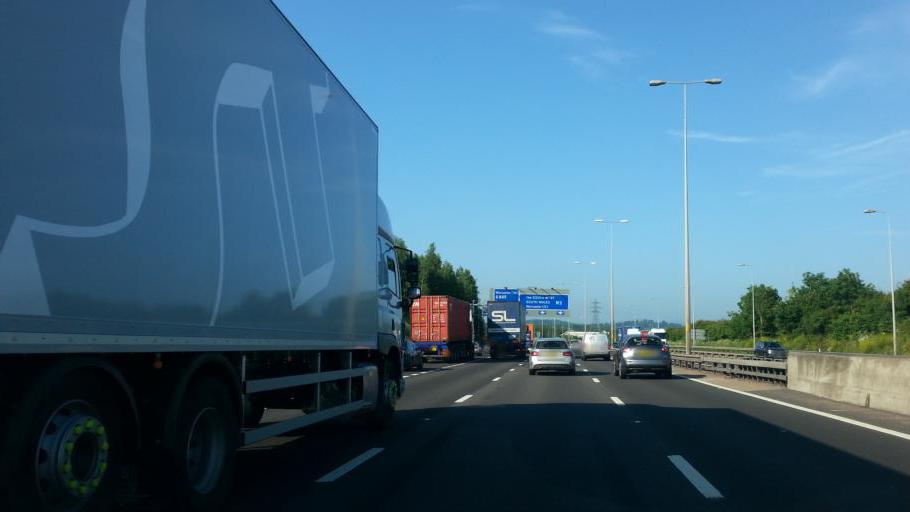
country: GB
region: England
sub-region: Worcestershire
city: Fernhill Heath
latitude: 52.2189
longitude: -2.1522
